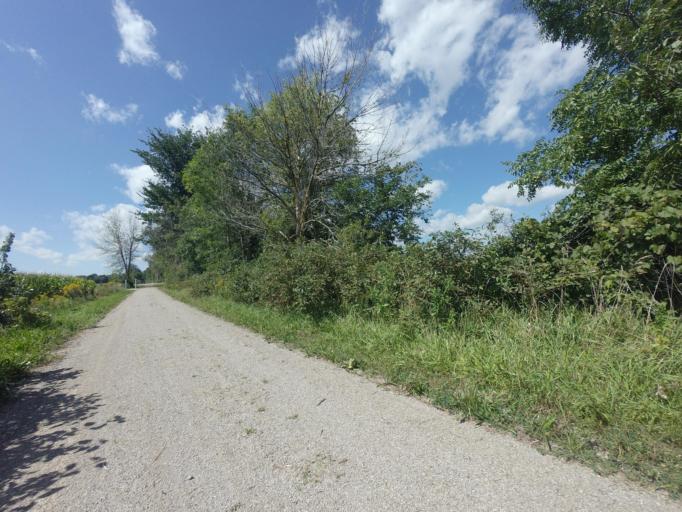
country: CA
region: Ontario
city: Huron East
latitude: 43.6710
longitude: -81.2771
